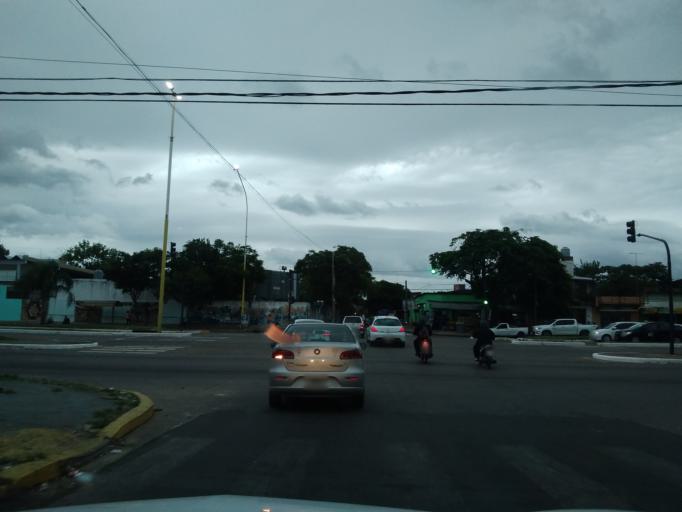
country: AR
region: Corrientes
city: Corrientes
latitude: -27.4769
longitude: -58.8250
